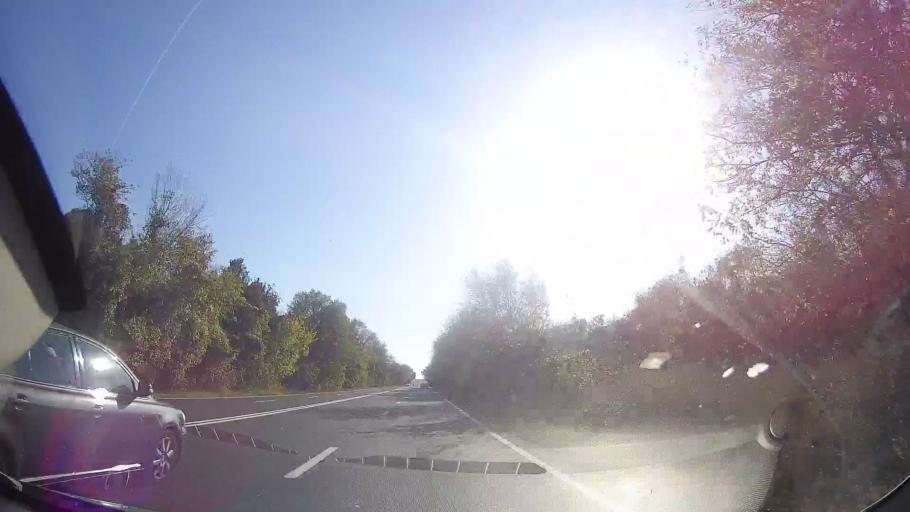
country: RO
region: Constanta
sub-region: Comuna Douazeci si Trei August
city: Dulcesti
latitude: 43.8650
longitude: 28.5751
